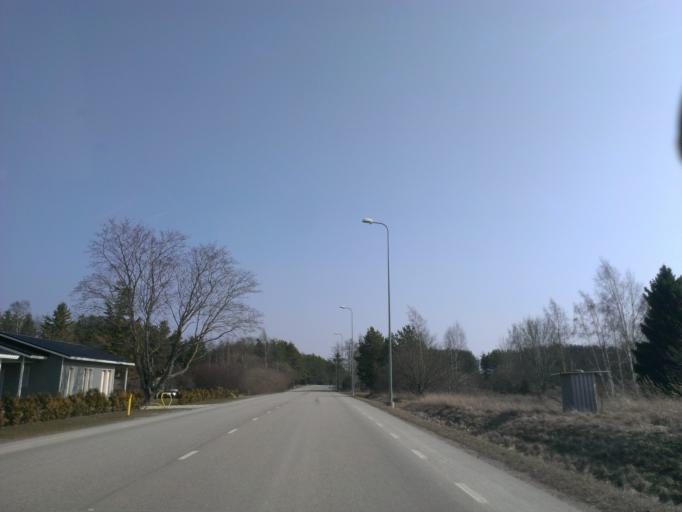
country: EE
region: Saare
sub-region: Orissaare vald
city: Orissaare
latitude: 58.5576
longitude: 23.0903
